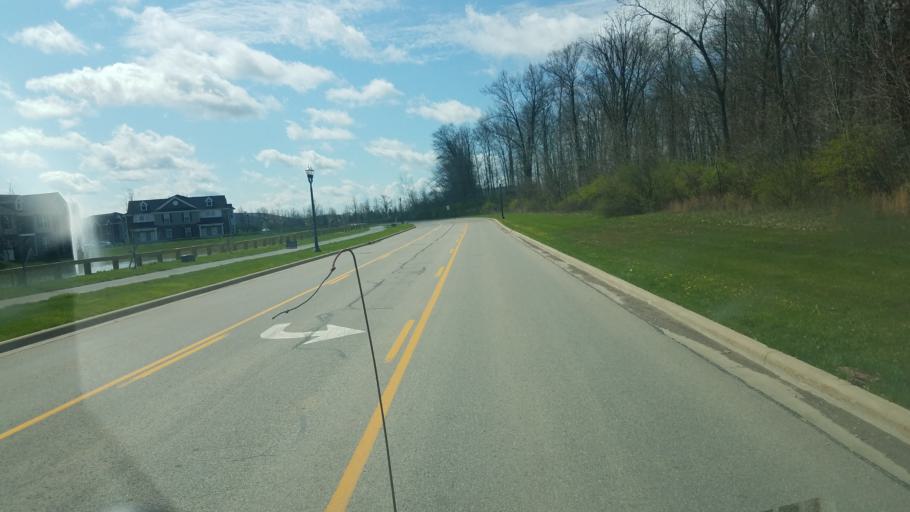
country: US
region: Ohio
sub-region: Delaware County
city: Delaware
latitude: 40.2921
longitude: -83.1145
